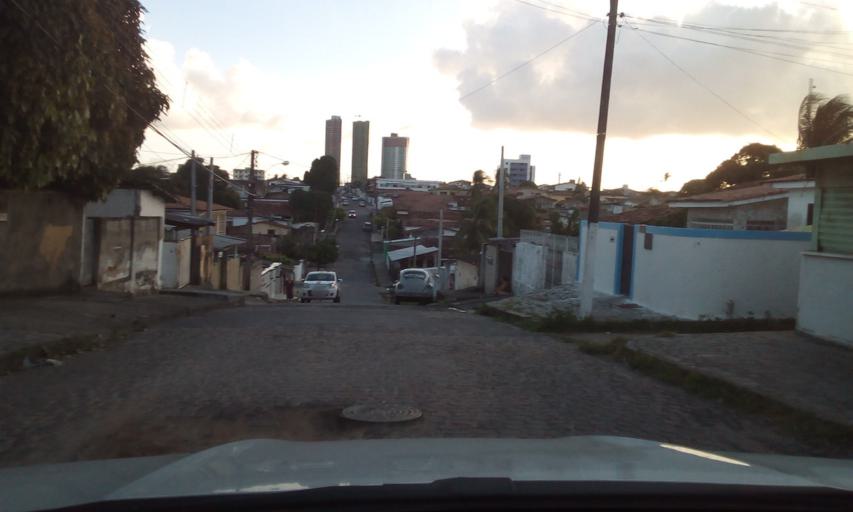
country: BR
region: Paraiba
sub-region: Joao Pessoa
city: Joao Pessoa
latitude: -7.1091
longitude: -34.8592
